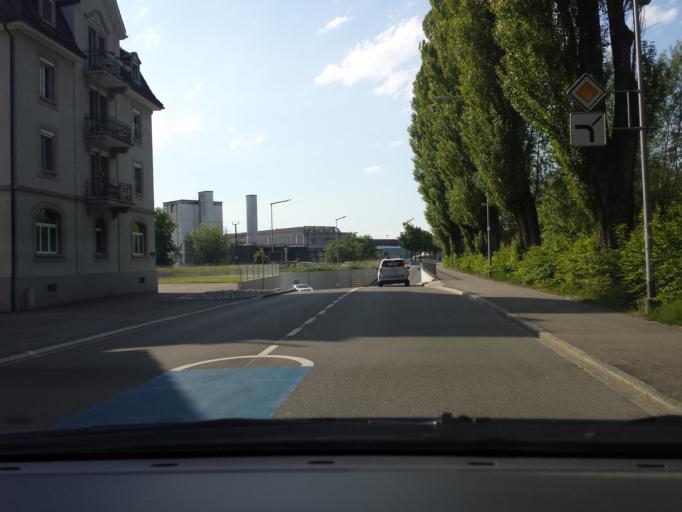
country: CH
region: Thurgau
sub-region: Arbon District
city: Arbon
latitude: 47.5052
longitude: 9.4358
